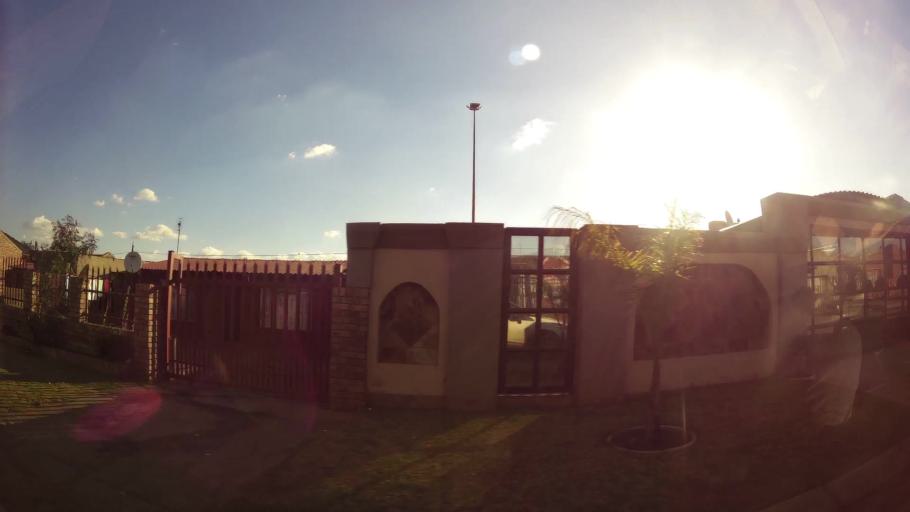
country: ZA
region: Mpumalanga
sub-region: Nkangala District Municipality
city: Witbank
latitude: -25.8674
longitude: 29.1731
